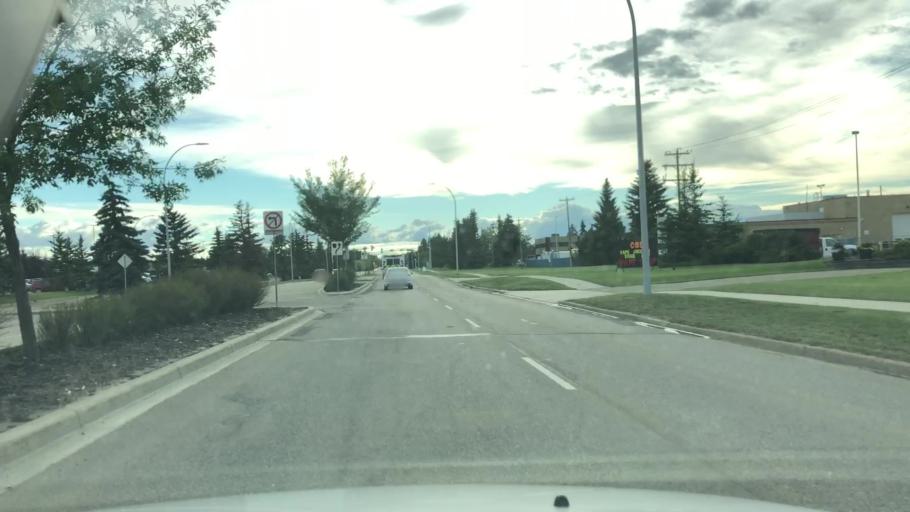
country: CA
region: Alberta
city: St. Albert
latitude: 53.6361
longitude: -113.5705
